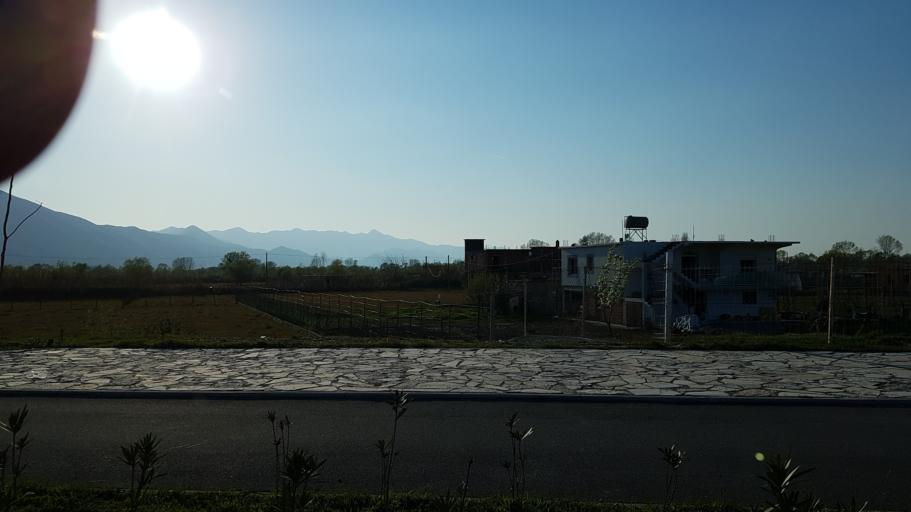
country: AL
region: Shkoder
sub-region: Rrethi i Shkodres
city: Shkoder
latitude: 42.0745
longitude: 19.4900
